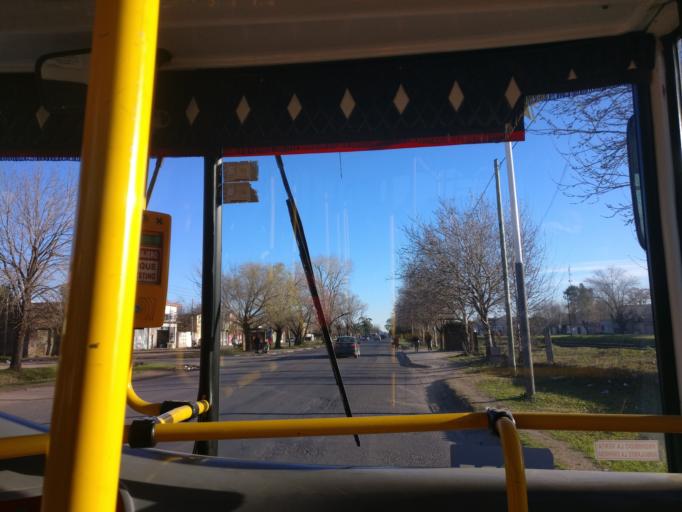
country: AR
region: Buenos Aires
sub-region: Partido de Ezeiza
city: Ezeiza
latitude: -34.9078
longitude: -58.5910
